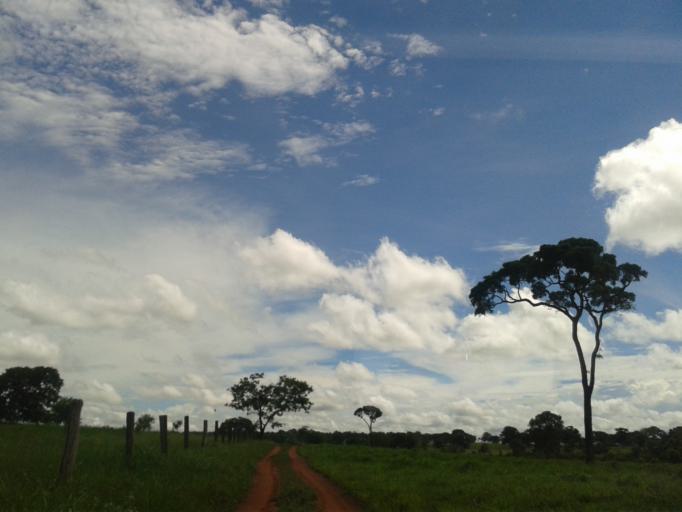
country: BR
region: Minas Gerais
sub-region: Santa Vitoria
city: Santa Vitoria
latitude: -19.1336
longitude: -50.4856
